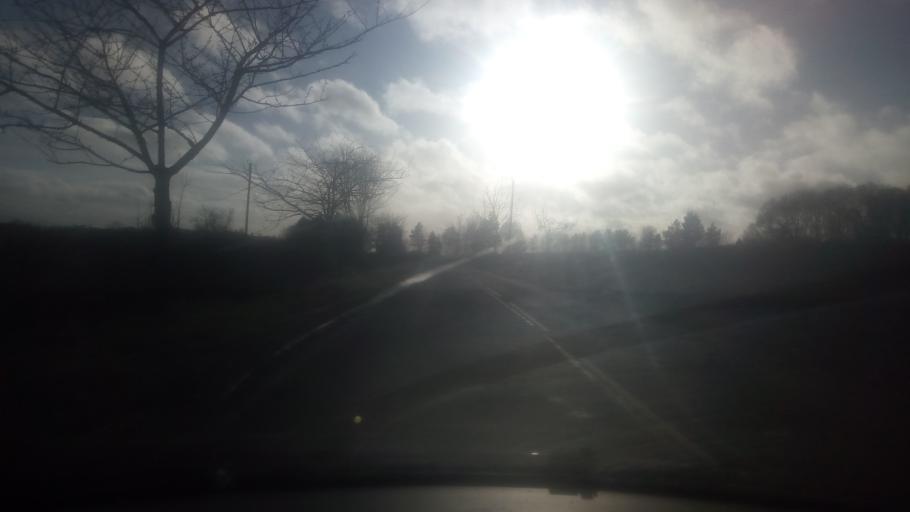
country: GB
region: Scotland
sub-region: The Scottish Borders
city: Duns
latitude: 55.6937
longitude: -2.3292
